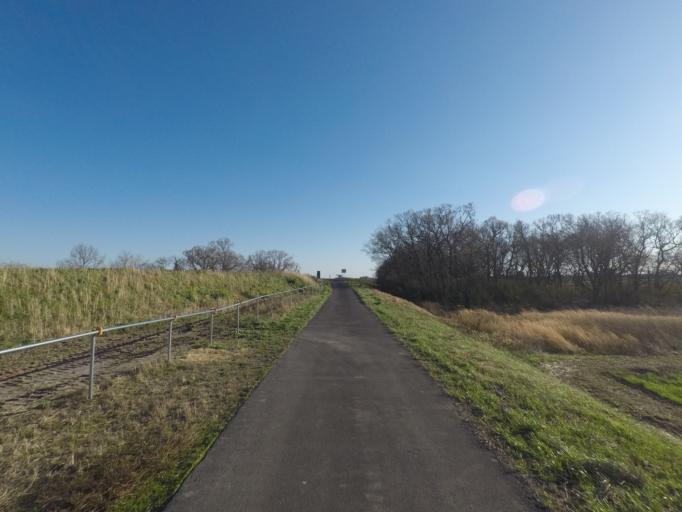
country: JP
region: Ibaraki
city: Ishige
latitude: 36.1729
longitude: 140.0066
